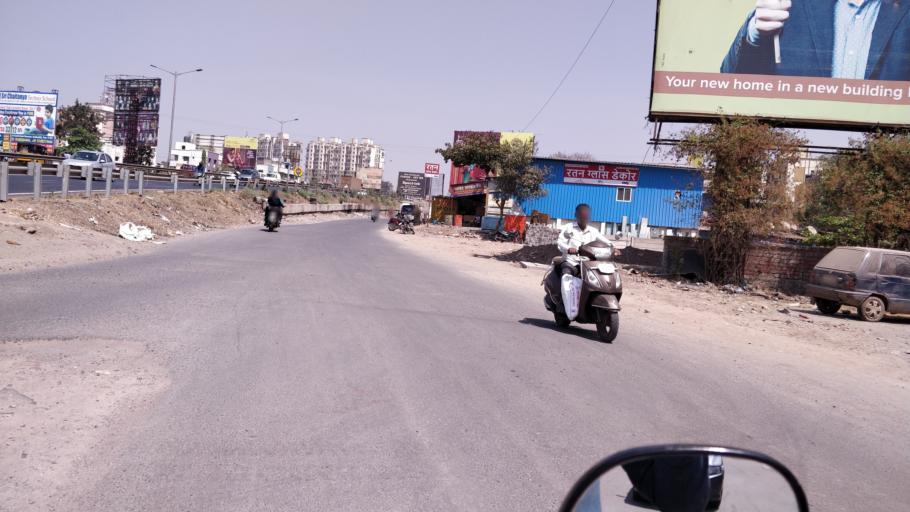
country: IN
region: Maharashtra
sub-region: Pune Division
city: Kharakvasla
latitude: 18.5138
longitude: 73.7699
